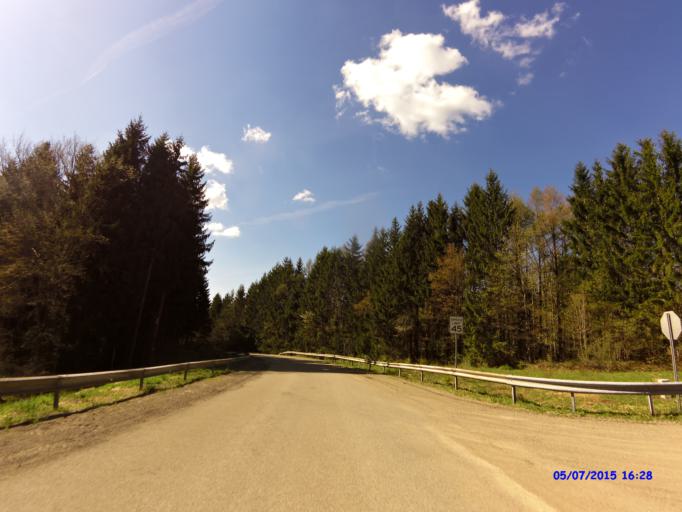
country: US
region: New York
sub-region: Cattaraugus County
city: Little Valley
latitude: 42.3129
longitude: -78.6816
